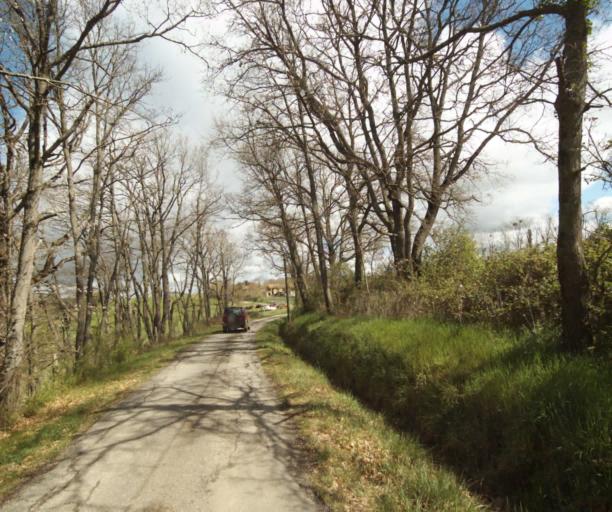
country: FR
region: Midi-Pyrenees
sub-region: Departement de l'Ariege
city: Saverdun
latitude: 43.2036
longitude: 1.5826
